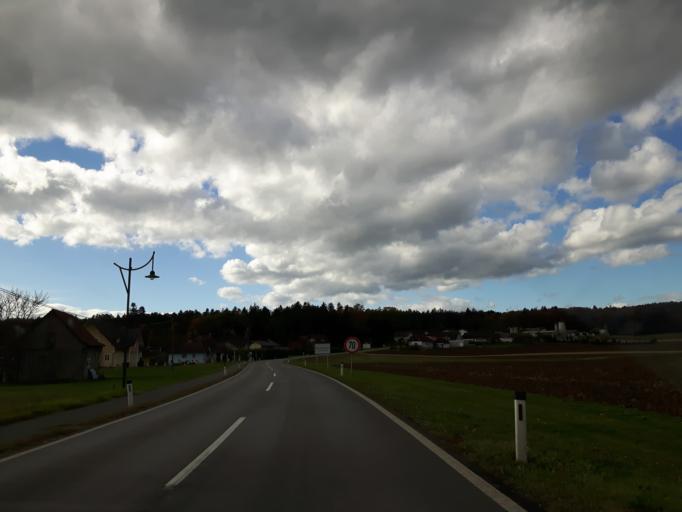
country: AT
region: Styria
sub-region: Politischer Bezirk Leibnitz
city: Hainsdorf im Schwarzautal
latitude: 46.8426
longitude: 15.6373
